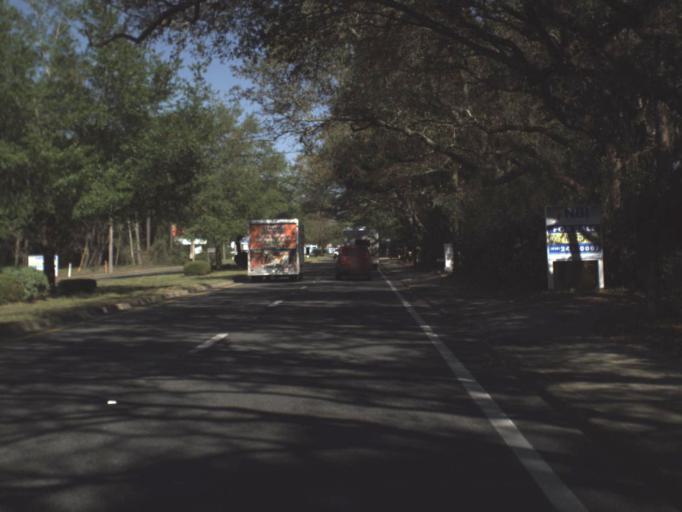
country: US
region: Florida
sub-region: Okaloosa County
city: Mary Esther
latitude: 30.4080
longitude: -86.6427
